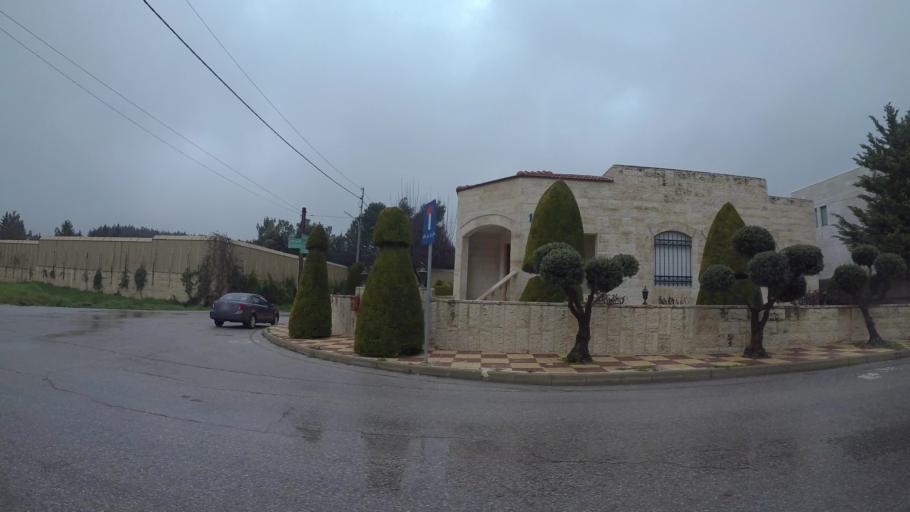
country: JO
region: Amman
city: Al Jubayhah
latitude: 32.0039
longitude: 35.8185
